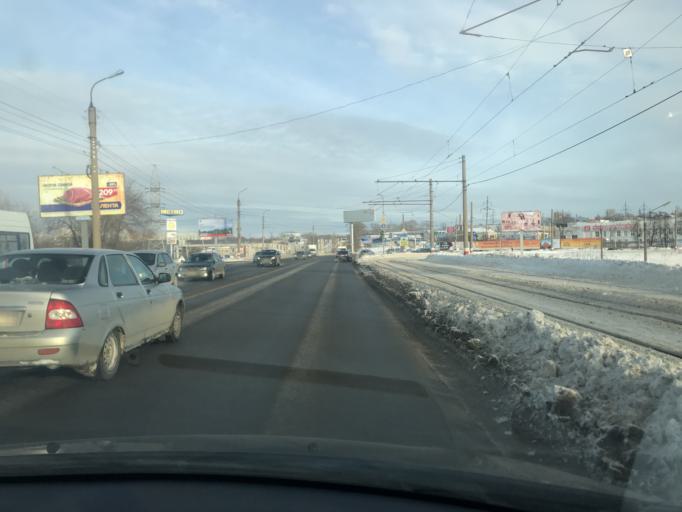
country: RU
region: Ulyanovsk
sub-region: Ulyanovskiy Rayon
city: Ulyanovsk
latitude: 54.3258
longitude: 48.3573
